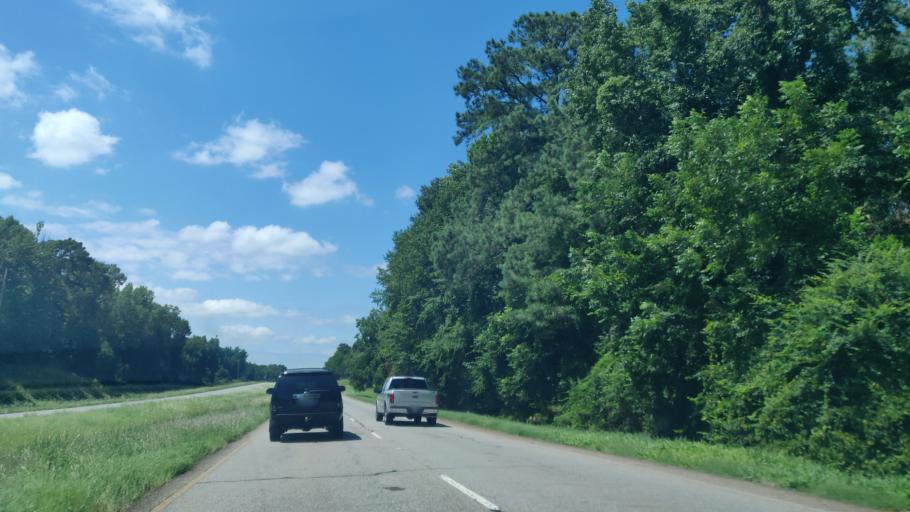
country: US
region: Georgia
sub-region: Stewart County
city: Richland
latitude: 32.0507
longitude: -84.6722
